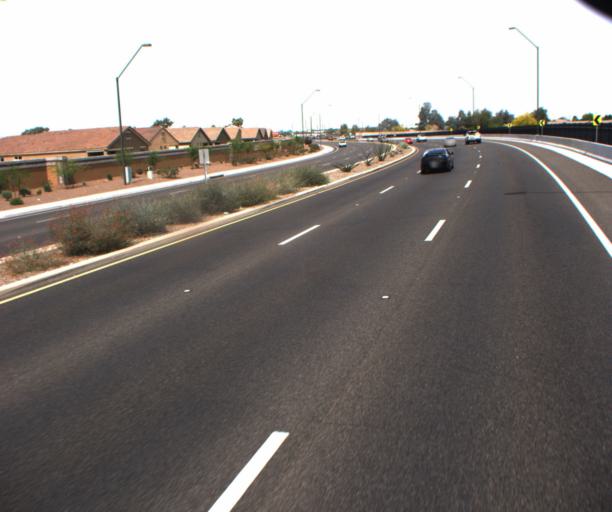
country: US
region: Arizona
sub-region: Maricopa County
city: Peoria
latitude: 33.5901
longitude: -112.2477
